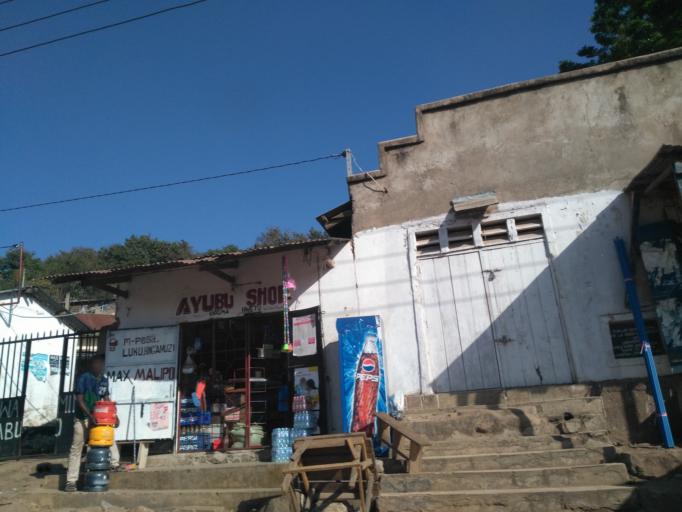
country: TZ
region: Mwanza
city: Mwanza
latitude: -2.5026
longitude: 32.8917
